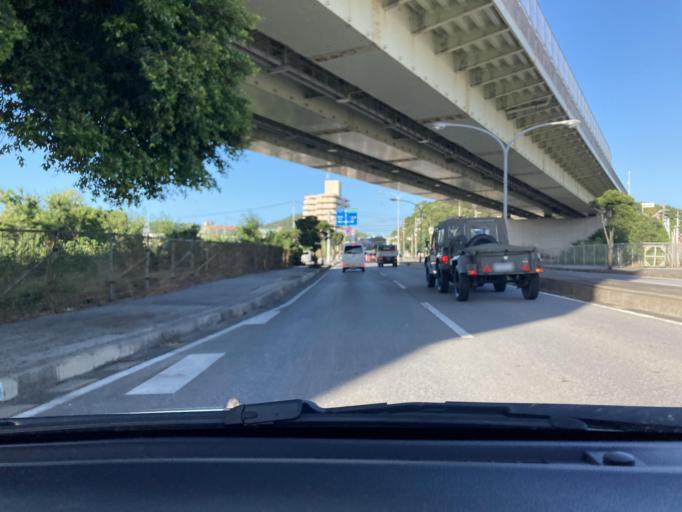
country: JP
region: Okinawa
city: Tomigusuku
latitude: 26.1793
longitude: 127.7152
